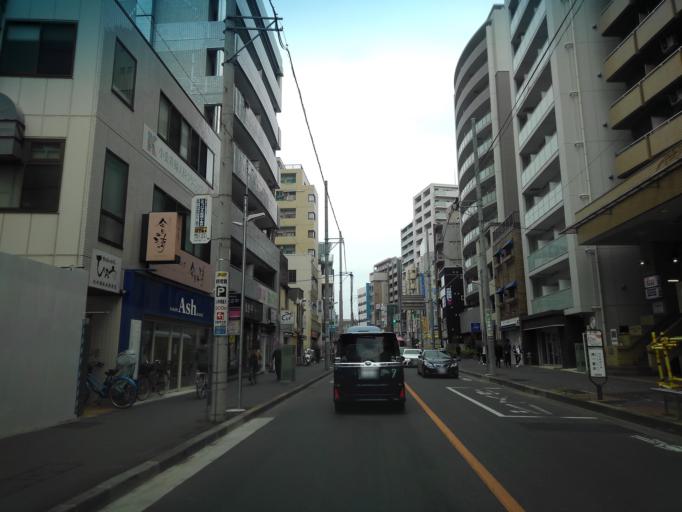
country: JP
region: Tokyo
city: Kokubunji
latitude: 35.6990
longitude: 139.5066
